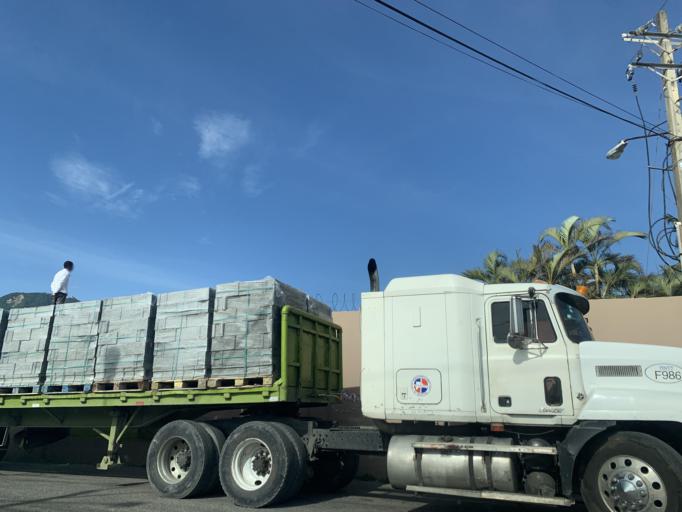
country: DO
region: Puerto Plata
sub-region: Puerto Plata
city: Puerto Plata
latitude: 19.8003
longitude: -70.6975
